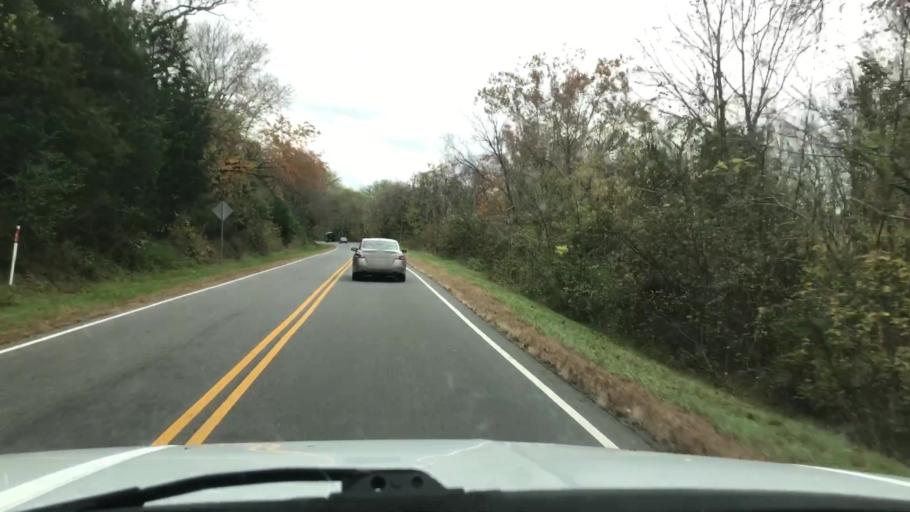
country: US
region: Virginia
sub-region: Goochland County
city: Goochland
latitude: 37.6203
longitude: -77.7667
